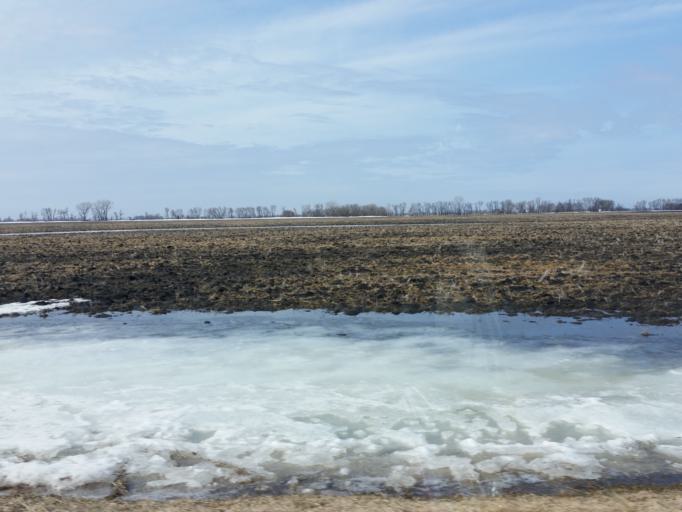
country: US
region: North Dakota
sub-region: Walsh County
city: Grafton
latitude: 48.3440
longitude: -97.2111
